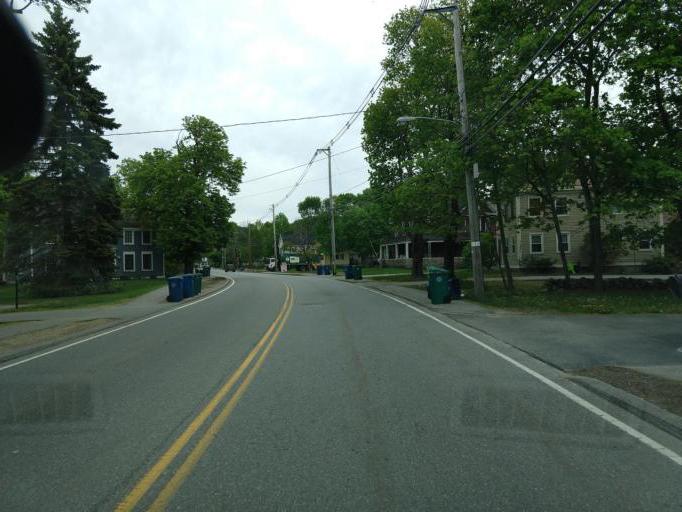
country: US
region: Massachusetts
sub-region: Middlesex County
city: Billerica
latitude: 42.5610
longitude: -71.2662
